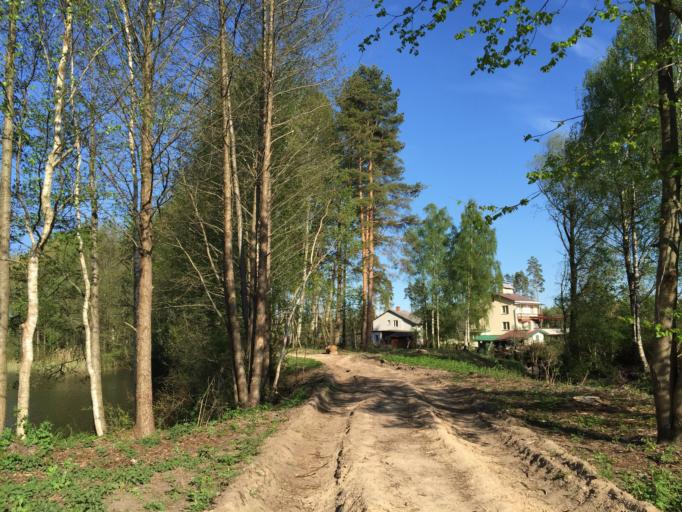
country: LV
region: Lecava
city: Iecava
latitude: 56.6935
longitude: 24.1002
